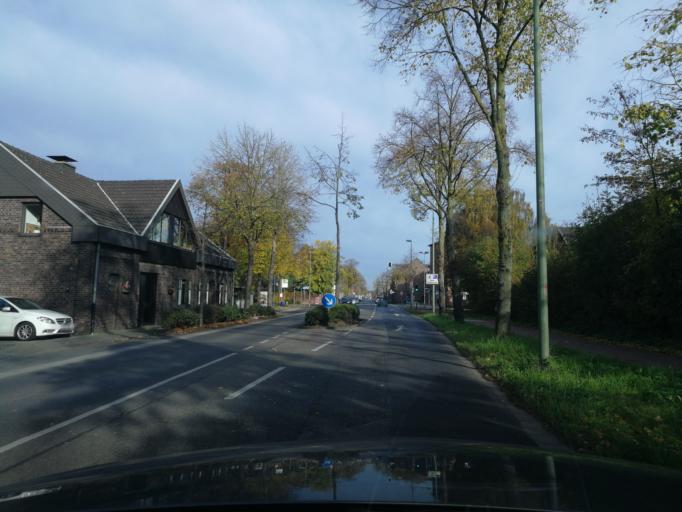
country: DE
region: North Rhine-Westphalia
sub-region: Regierungsbezirk Dusseldorf
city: Meerbusch
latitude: 51.3037
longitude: 6.6719
